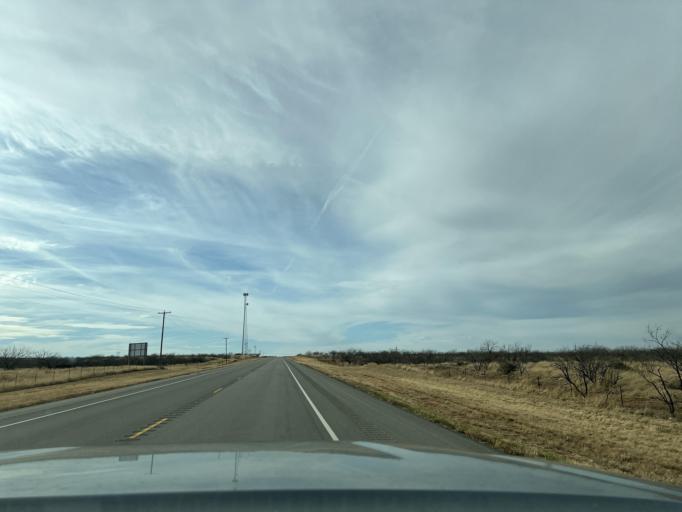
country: US
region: Texas
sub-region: Jones County
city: Anson
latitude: 32.7507
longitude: -99.7201
